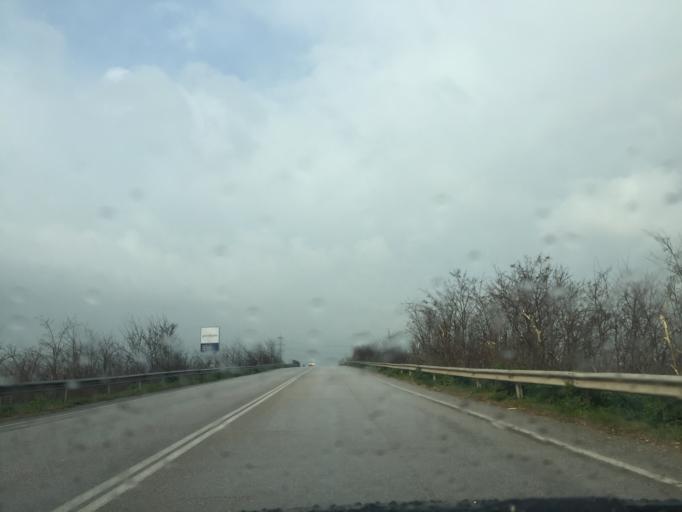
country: IT
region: Apulia
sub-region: Provincia di Foggia
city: Foggia
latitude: 41.4982
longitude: 15.5344
